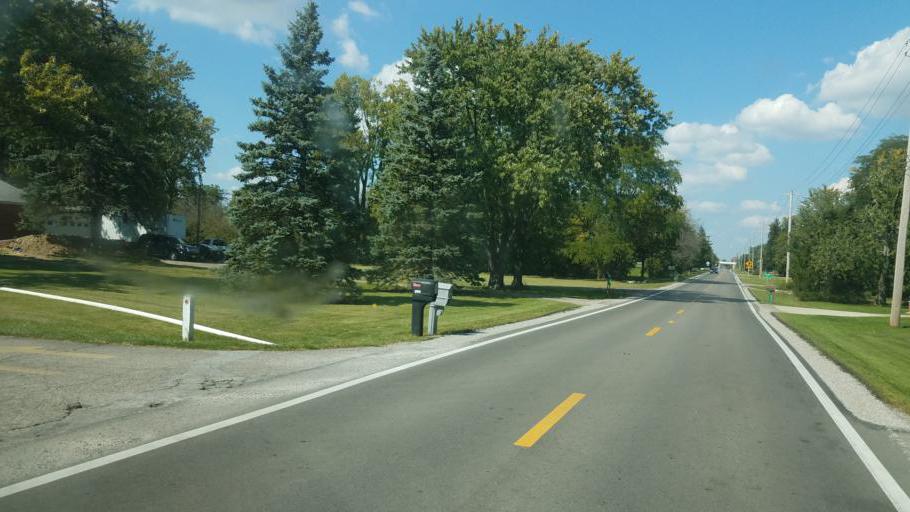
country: US
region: Ohio
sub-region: Franklin County
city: Grove City
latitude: 39.9046
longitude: -83.1082
